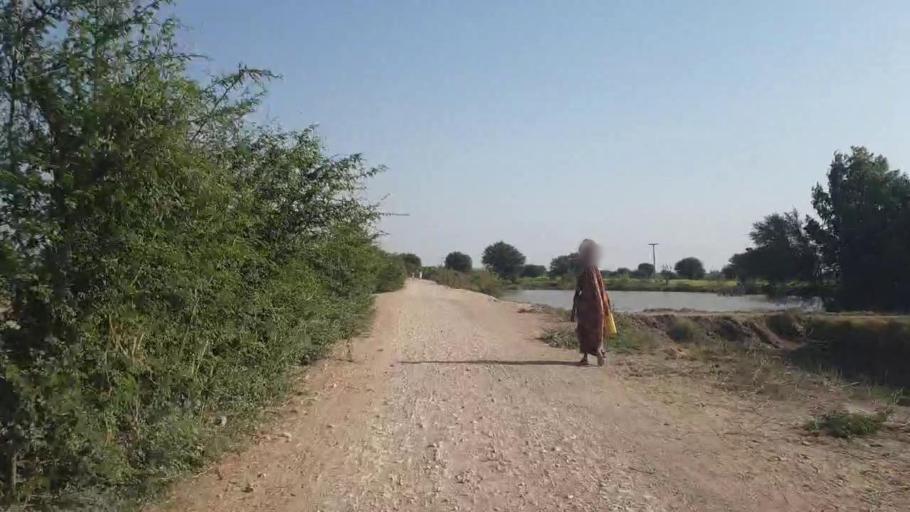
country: PK
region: Sindh
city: Chor
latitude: 25.5200
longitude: 69.6741
